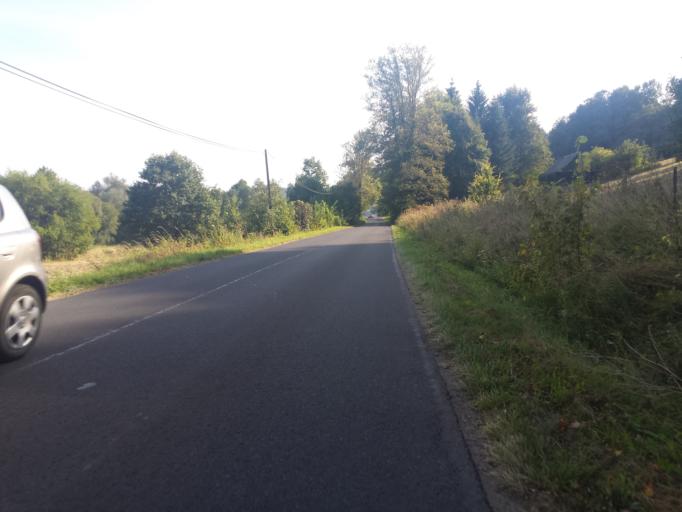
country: PL
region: Subcarpathian Voivodeship
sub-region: Powiat leski
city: Uherce Mineralne
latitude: 49.4564
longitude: 22.3920
